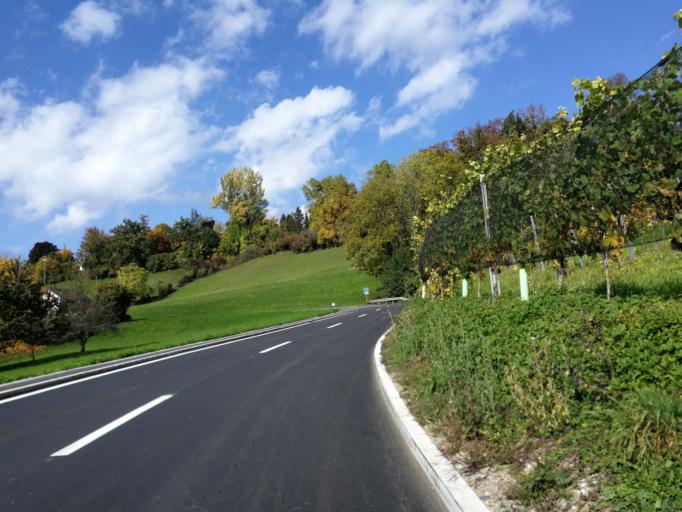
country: CH
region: Zurich
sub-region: Bezirk Meilen
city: Uetikon / Grossdorf
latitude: 47.2706
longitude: 8.6728
